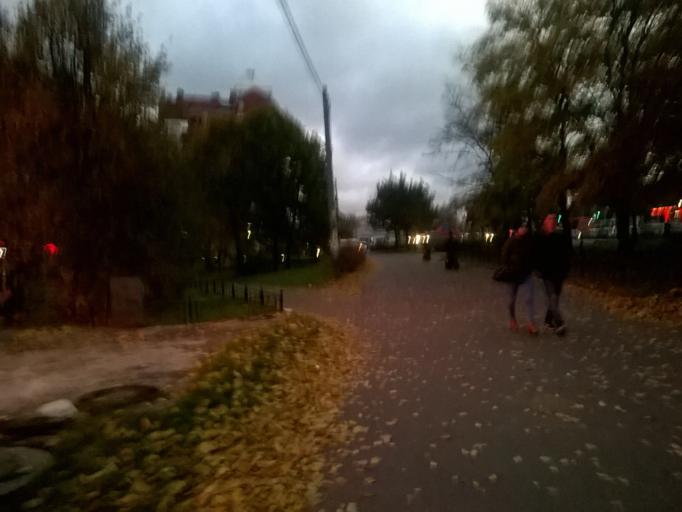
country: RU
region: St.-Petersburg
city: Ozerki
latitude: 60.0355
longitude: 30.3228
